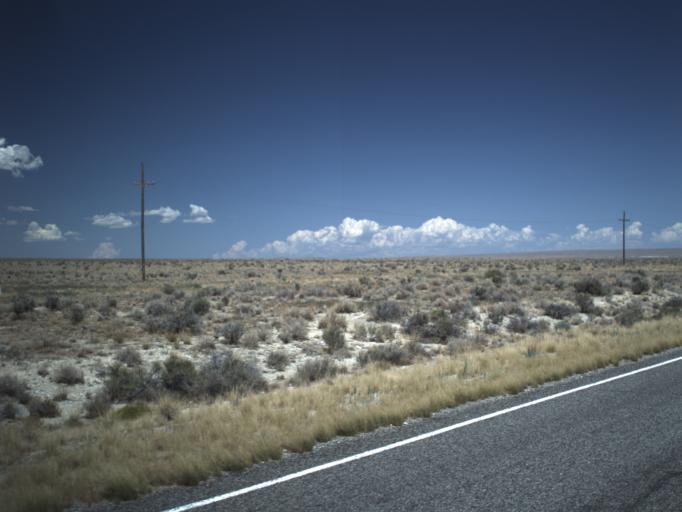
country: US
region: Utah
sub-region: Beaver County
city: Milford
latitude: 39.0668
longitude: -113.2306
